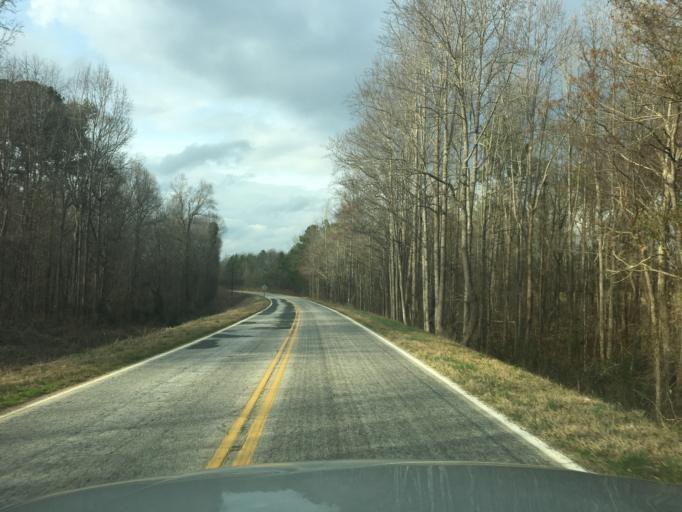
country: US
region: South Carolina
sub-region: Abbeville County
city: Due West
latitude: 34.2690
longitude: -82.4191
